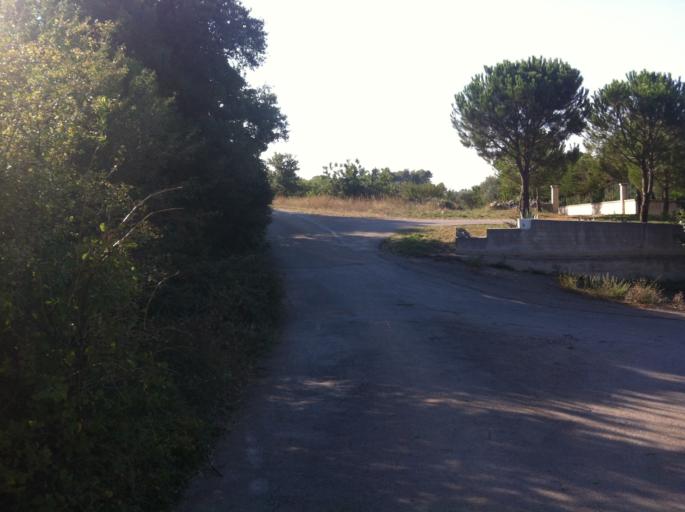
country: IT
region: Apulia
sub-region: Provincia di Bari
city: Noci
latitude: 40.8215
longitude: 17.1493
